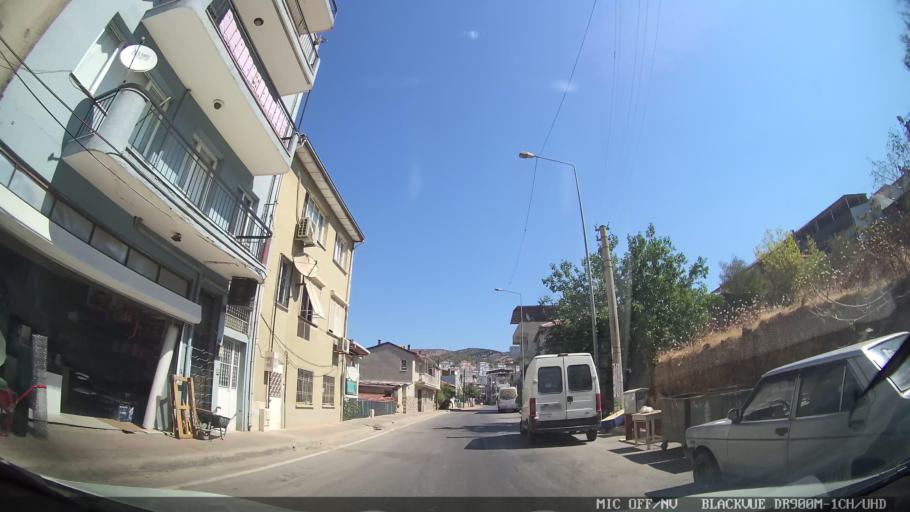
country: TR
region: Izmir
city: Karsiyaka
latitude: 38.4952
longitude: 27.0663
